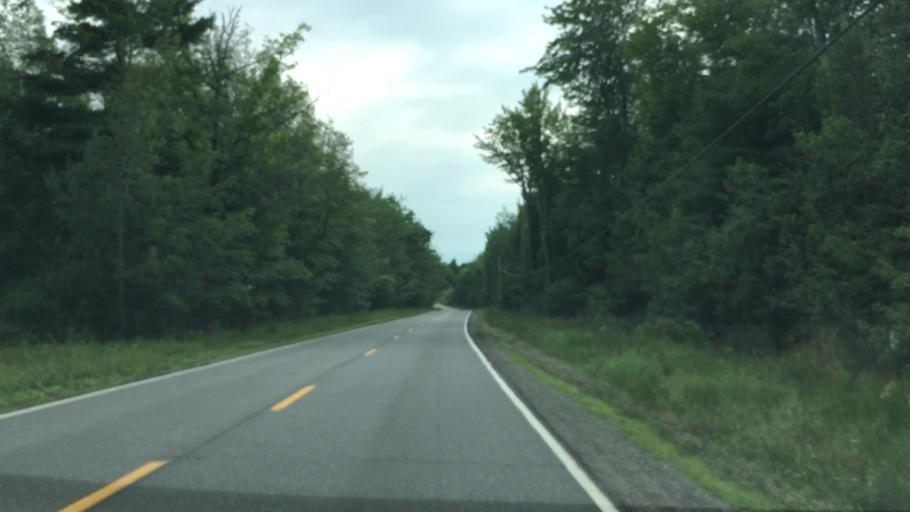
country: US
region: Maine
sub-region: Waldo County
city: Belfast
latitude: 44.3716
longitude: -69.0344
